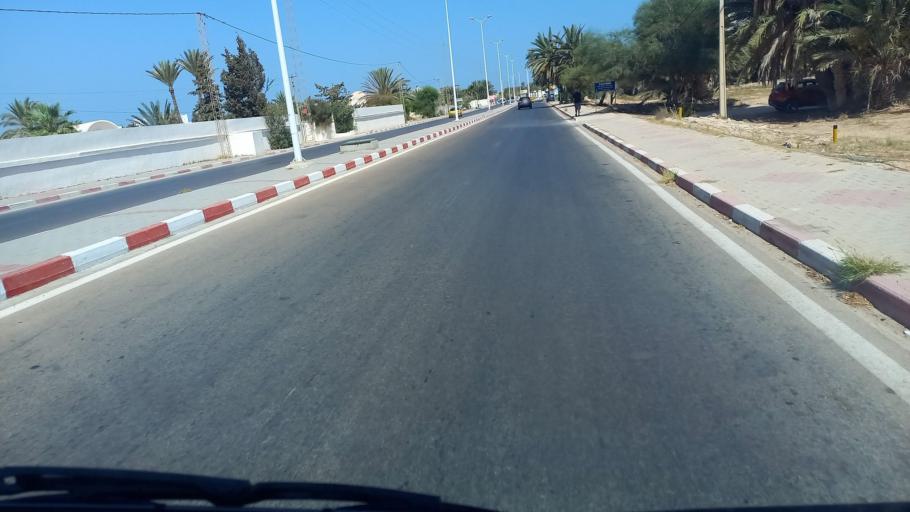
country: TN
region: Madanin
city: Midoun
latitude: 33.8654
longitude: 10.9613
